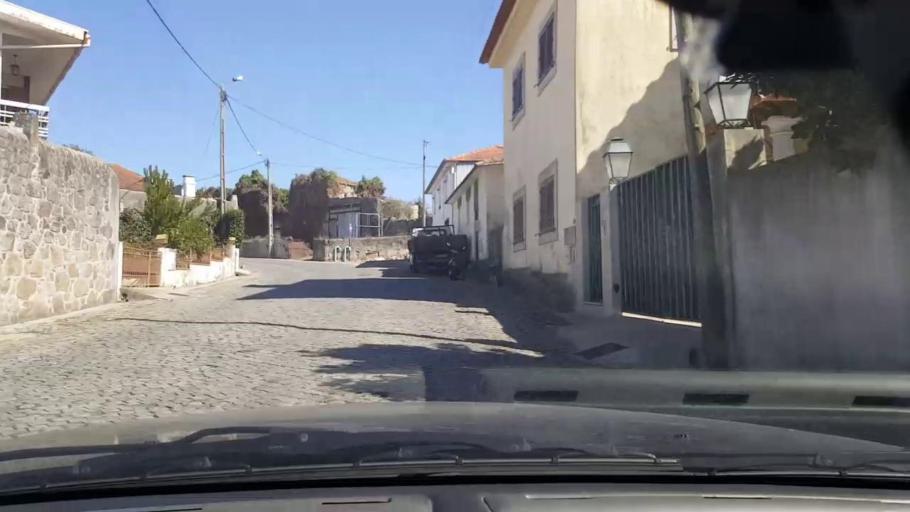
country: PT
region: Porto
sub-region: Maia
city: Gemunde
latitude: 41.3069
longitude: -8.6575
